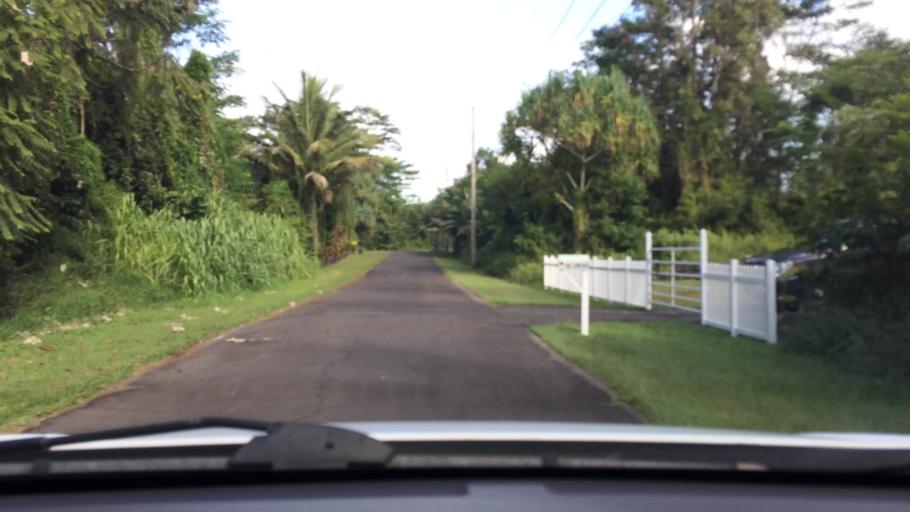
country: US
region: Hawaii
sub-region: Hawaii County
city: Hawaiian Beaches
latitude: 19.5440
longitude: -154.8984
